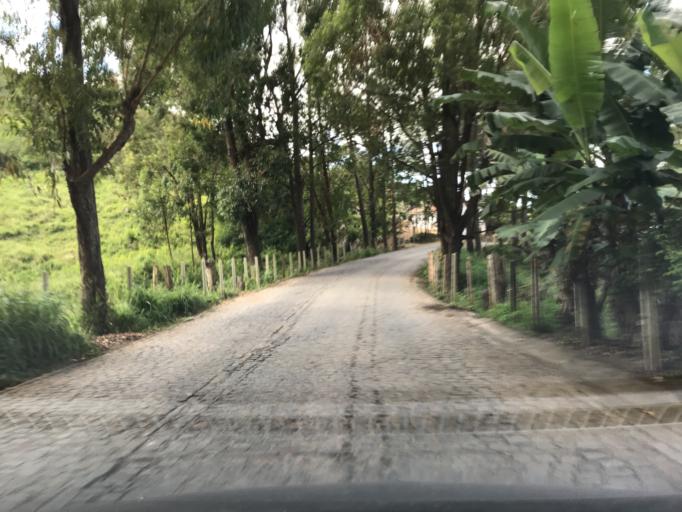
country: BR
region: Pernambuco
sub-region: Bezerros
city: Bezerros
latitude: -8.1833
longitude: -35.7694
